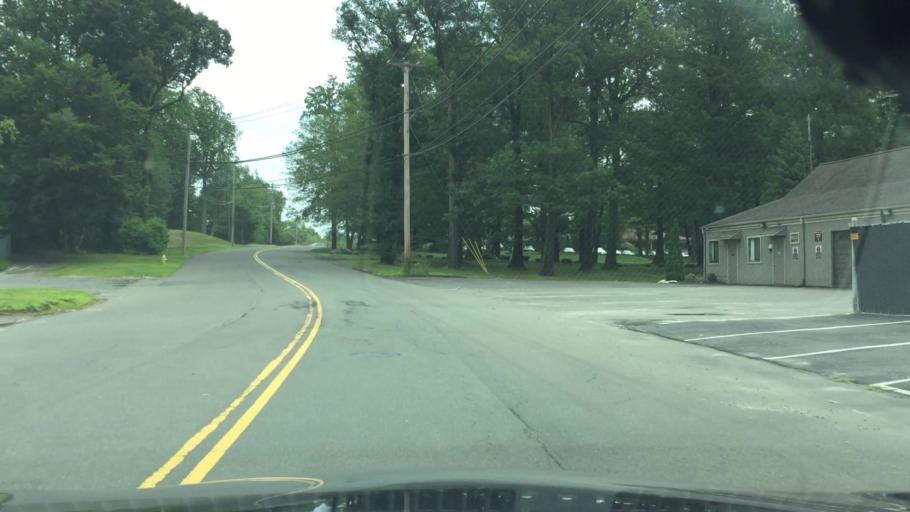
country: US
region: Connecticut
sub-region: New Haven County
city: City of Milford (balance)
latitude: 41.2508
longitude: -73.1163
